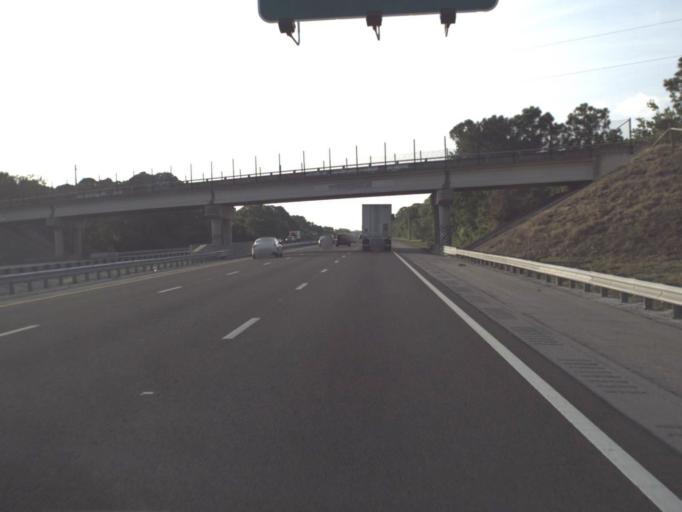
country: US
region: Florida
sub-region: Brevard County
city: Port Saint John
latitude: 28.4859
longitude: -80.8258
